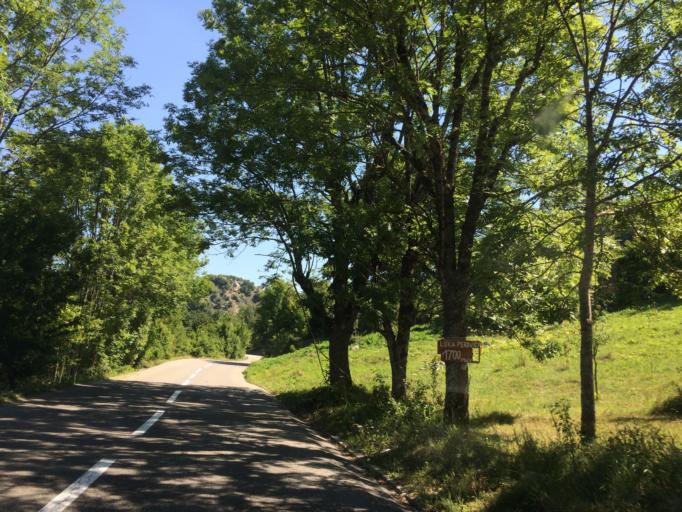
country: ME
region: Opstina Savnik
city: Savnik
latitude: 42.9476
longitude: 19.0796
